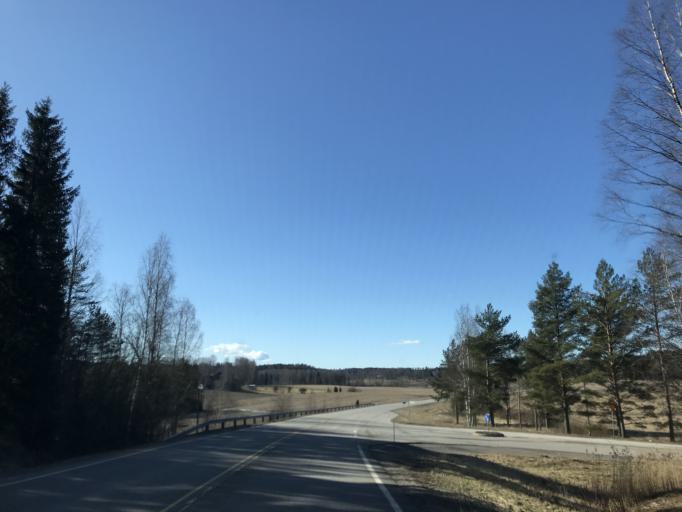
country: FI
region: Uusimaa
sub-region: Raaseporin
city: Pohja
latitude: 60.0938
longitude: 23.5098
